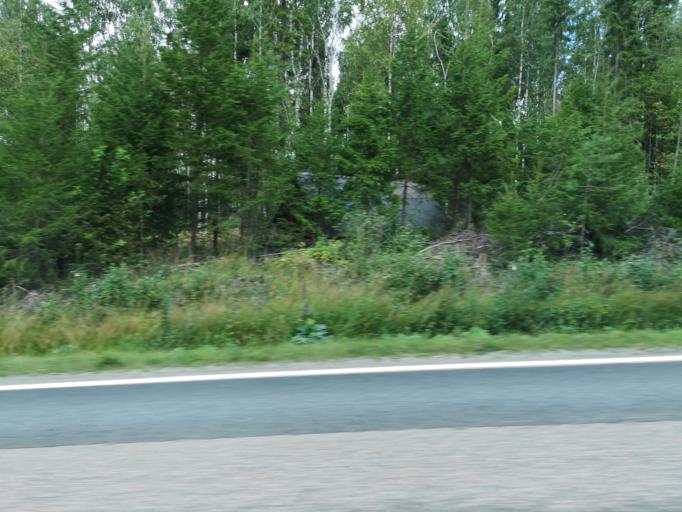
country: FI
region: Central Finland
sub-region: Jyvaeskylae
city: Hankasalmi
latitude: 62.3572
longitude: 26.4864
